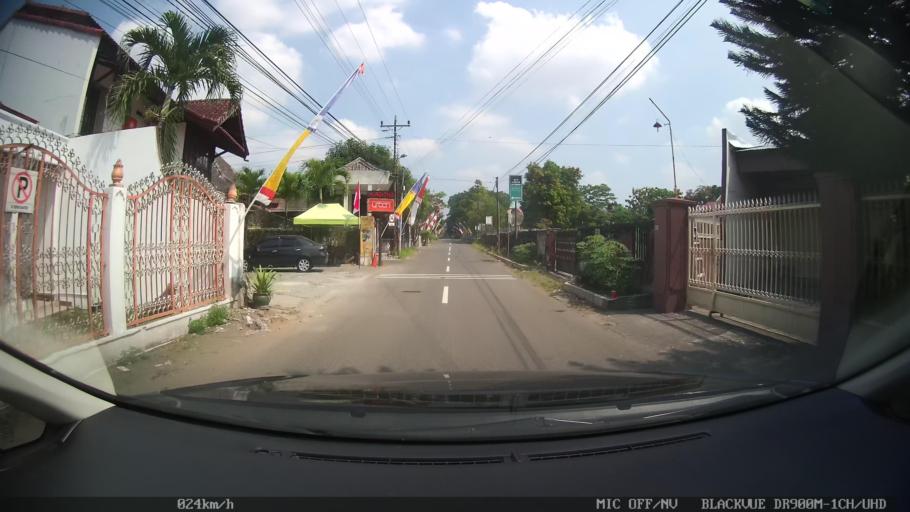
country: ID
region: Daerah Istimewa Yogyakarta
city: Yogyakarta
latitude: -7.7960
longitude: 110.3913
